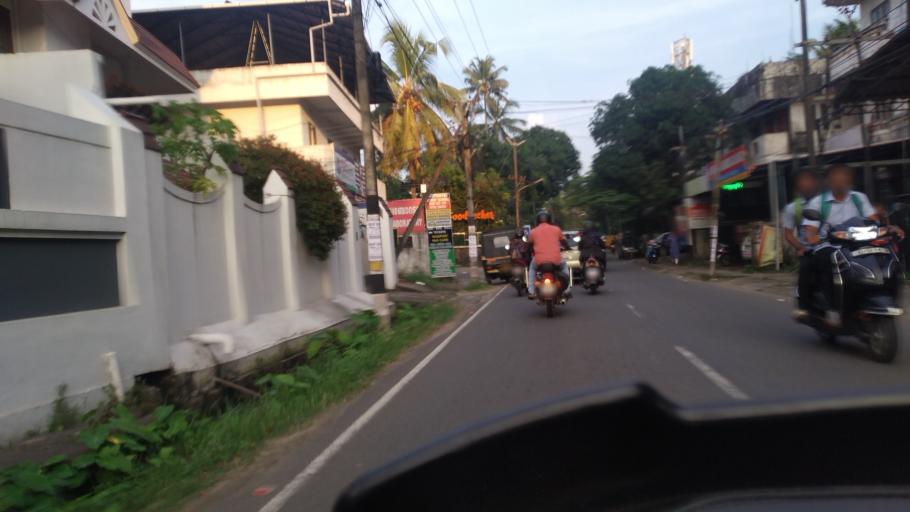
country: IN
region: Kerala
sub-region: Ernakulam
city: Elur
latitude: 10.0199
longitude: 76.2996
